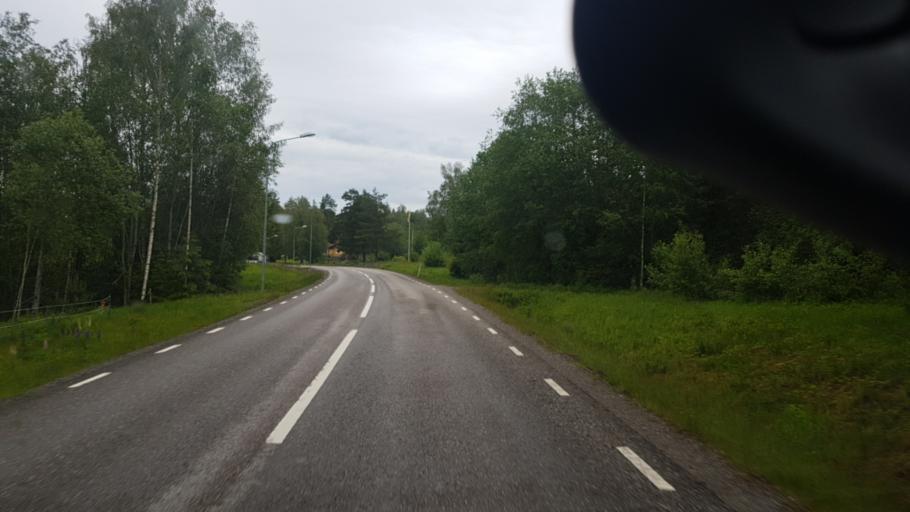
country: SE
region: Vaermland
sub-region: Eda Kommun
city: Amotfors
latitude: 59.6814
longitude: 12.1471
